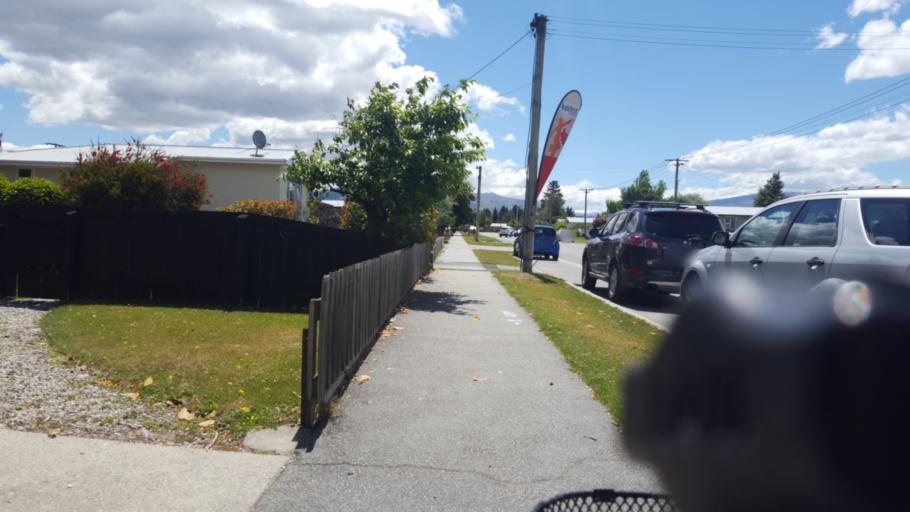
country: NZ
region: Otago
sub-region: Queenstown-Lakes District
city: Wanaka
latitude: -45.2433
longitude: 169.3909
